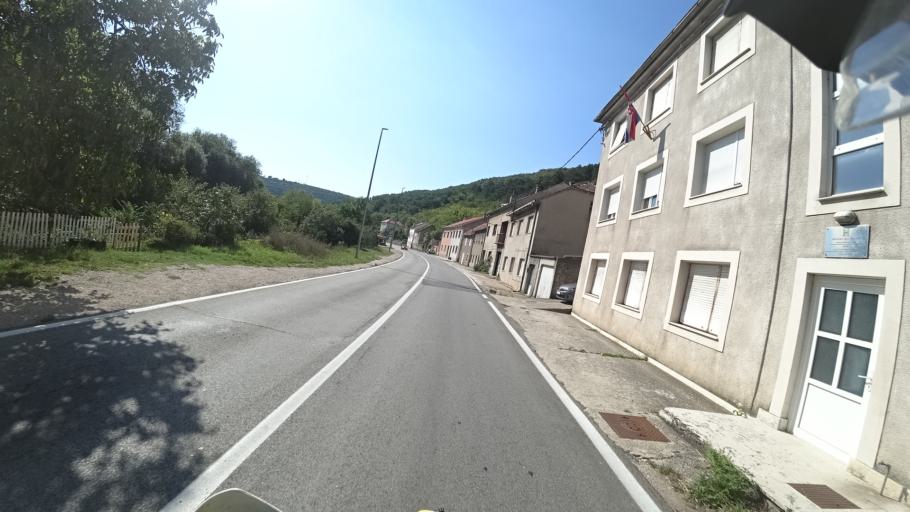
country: HR
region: Sibensko-Kniniska
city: Knin
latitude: 44.0320
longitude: 16.1896
